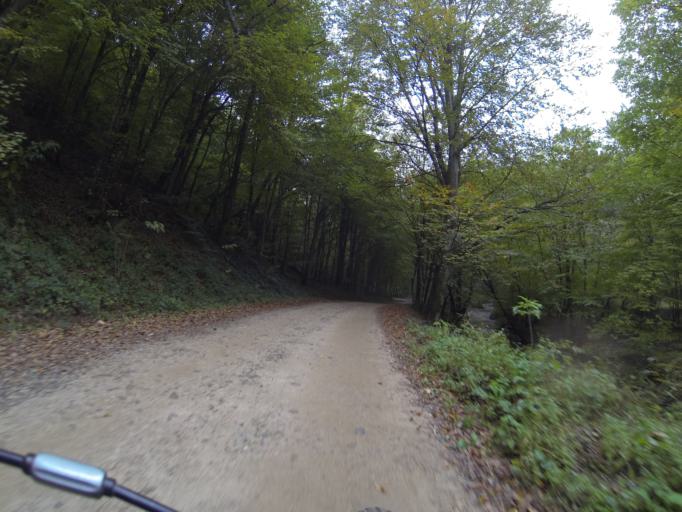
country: RO
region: Gorj
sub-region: Comuna Tismana
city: Pocruia
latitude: 45.0556
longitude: 22.9069
